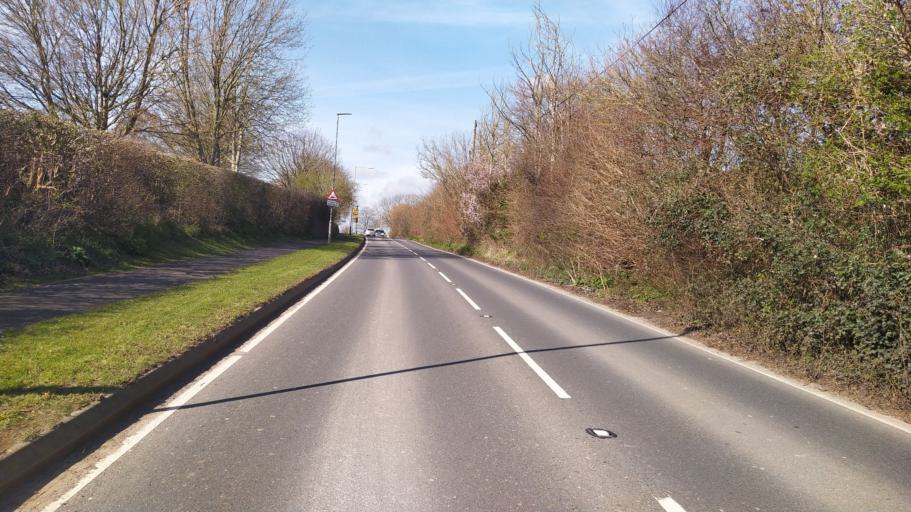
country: GB
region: England
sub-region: Somerset
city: Ilchester
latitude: 51.0090
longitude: -2.6789
